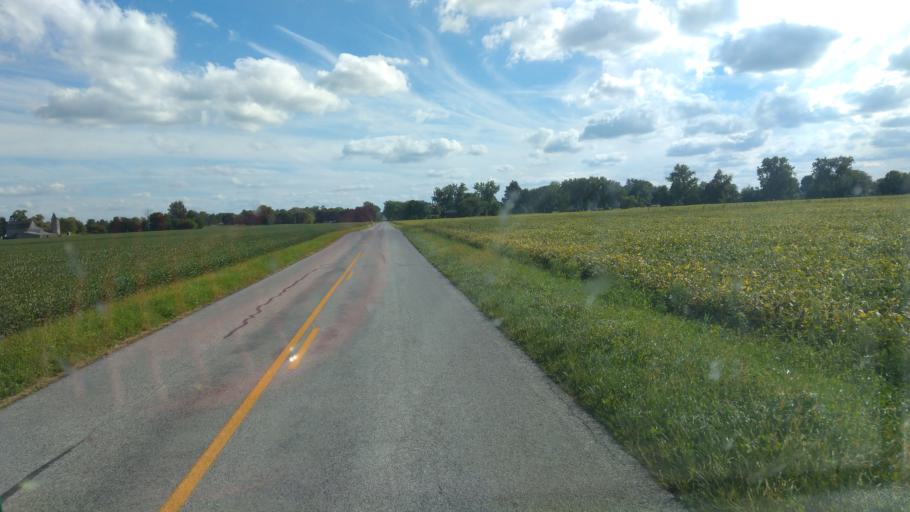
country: US
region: Ohio
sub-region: Sandusky County
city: Mount Carmel
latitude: 41.2761
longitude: -82.9558
